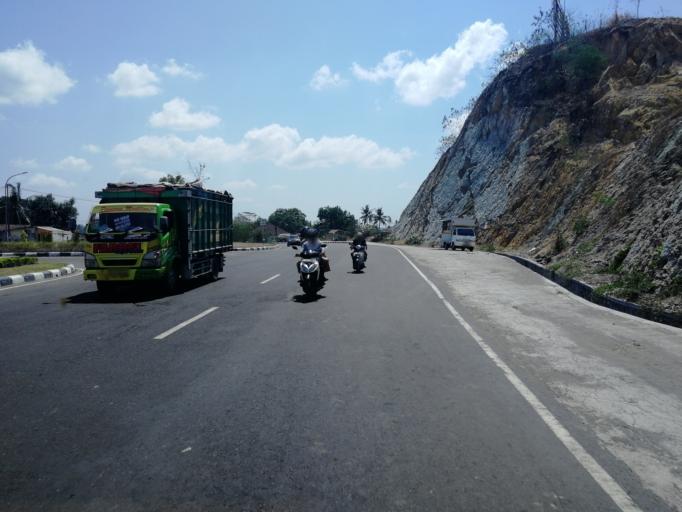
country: ID
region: West Nusa Tenggara
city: Jelateng Timur
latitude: -8.6920
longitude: 116.1114
